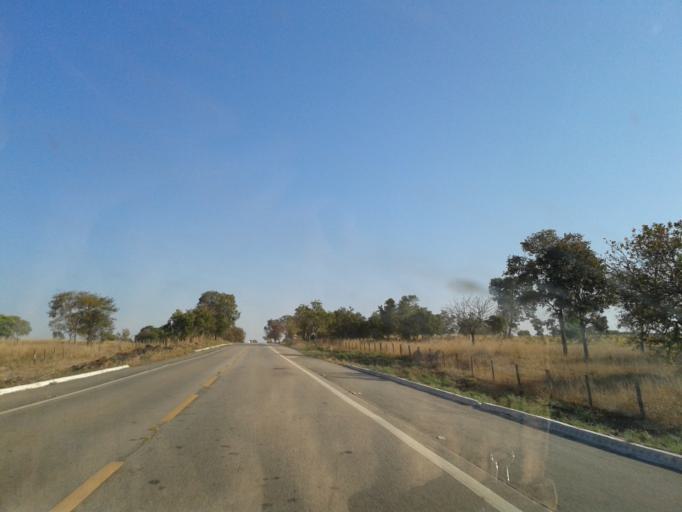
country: BR
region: Goias
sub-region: Mozarlandia
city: Mozarlandia
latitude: -15.2615
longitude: -50.4912
